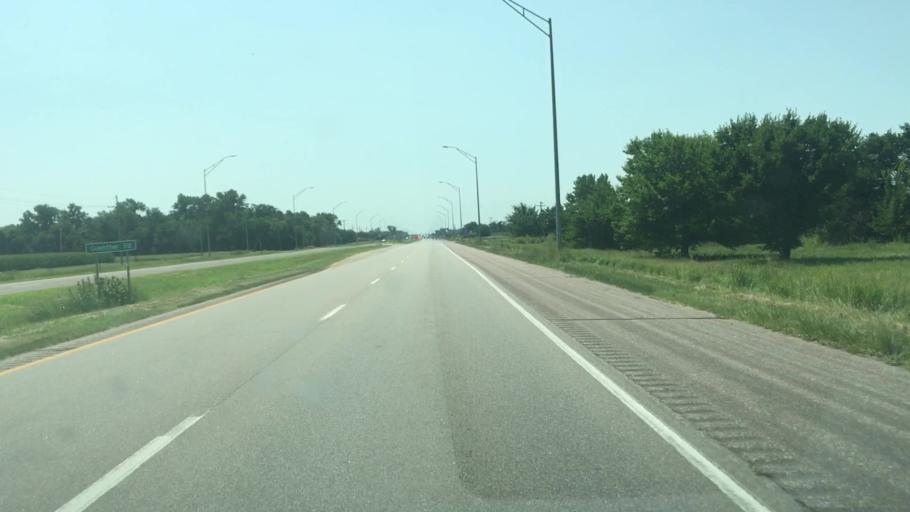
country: US
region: Nebraska
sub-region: Hall County
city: Grand Island
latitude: 40.8465
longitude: -98.3787
